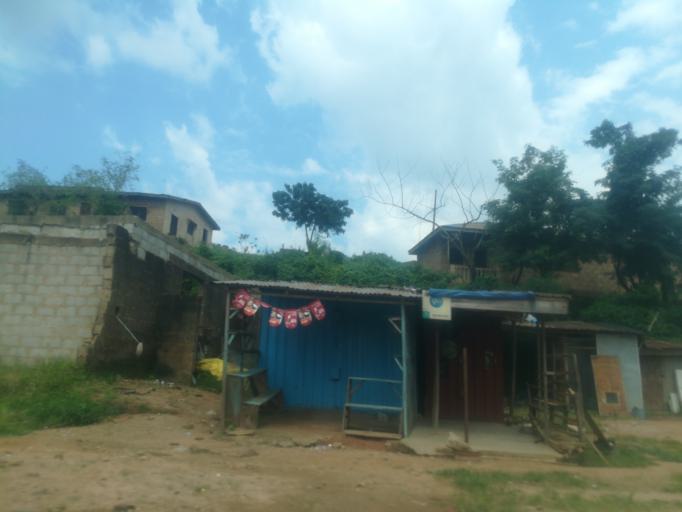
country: NG
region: Oyo
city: Ibadan
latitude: 7.4171
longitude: 3.8504
